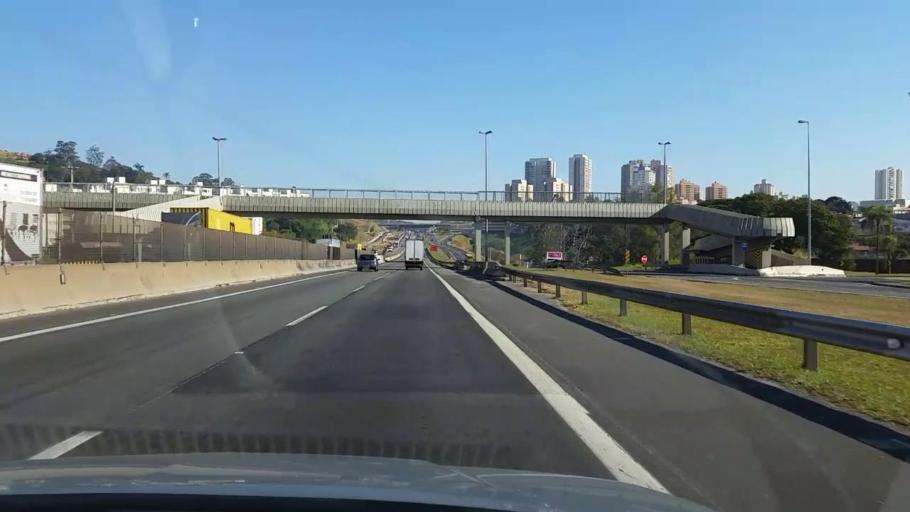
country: BR
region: Sao Paulo
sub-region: Jundiai
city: Jundiai
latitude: -23.2137
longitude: -46.8874
